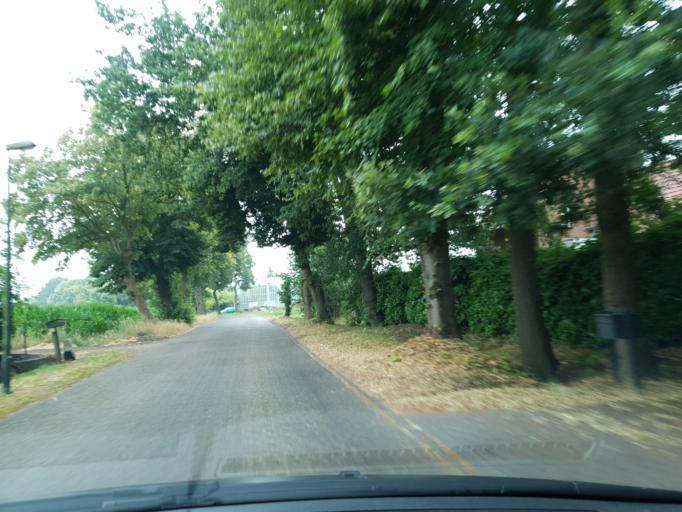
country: BE
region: Flanders
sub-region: Provincie Antwerpen
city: Beerse
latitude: 51.3452
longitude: 4.8352
